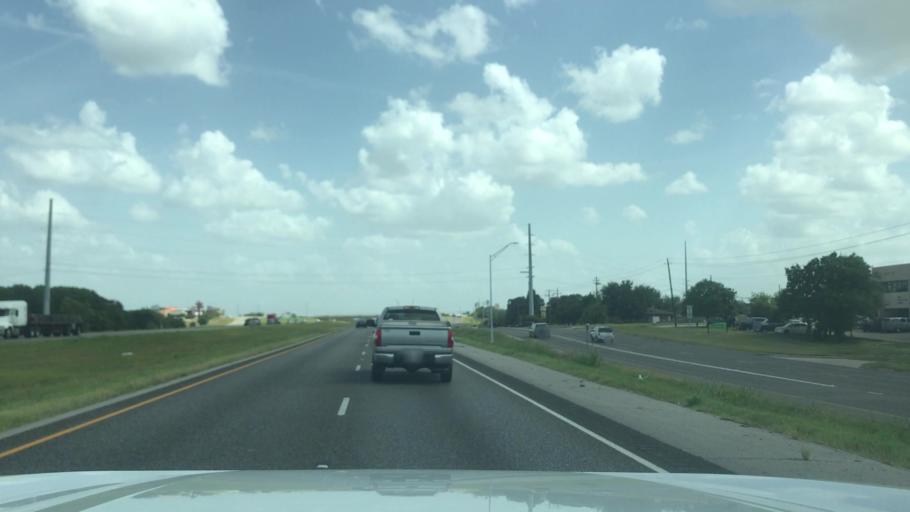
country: US
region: Texas
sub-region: Brazos County
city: Bryan
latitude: 30.6792
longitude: -96.3436
